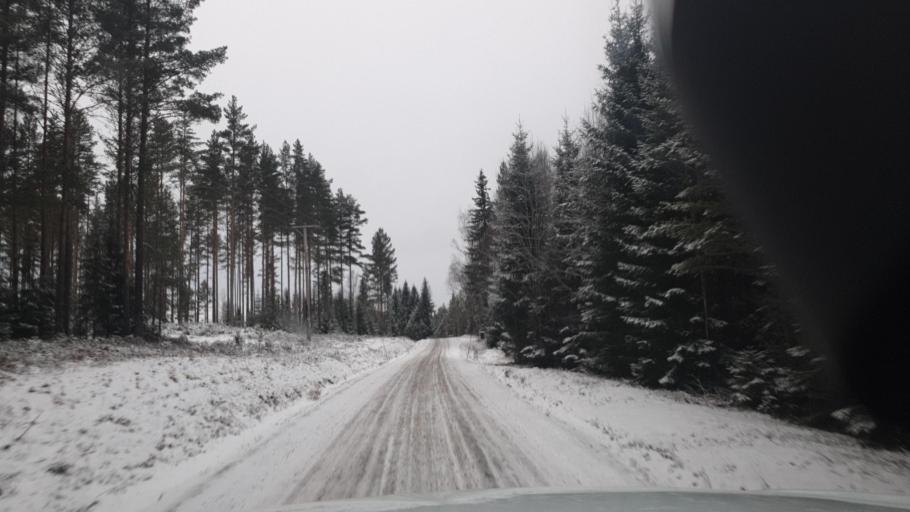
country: SE
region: Vaermland
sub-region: Sunne Kommun
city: Sunne
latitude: 59.6476
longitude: 13.0564
